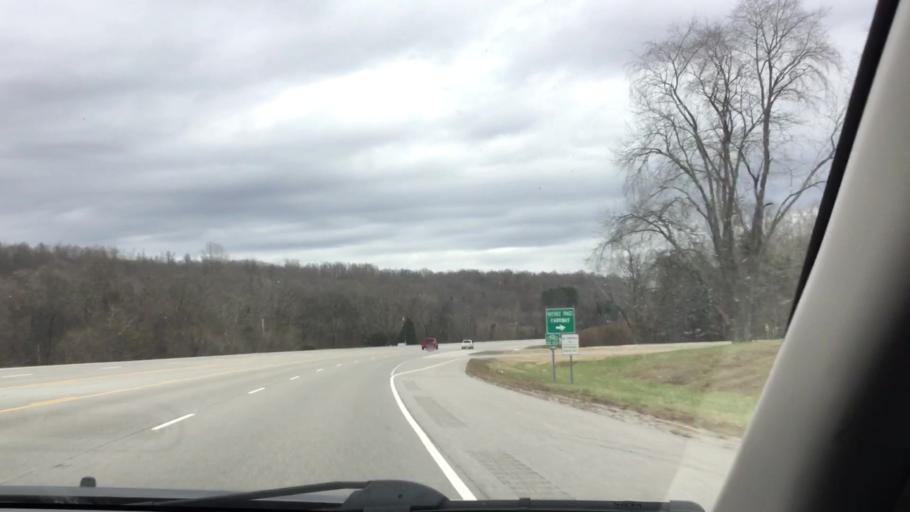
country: US
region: Tennessee
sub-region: Lewis County
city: Hohenwald
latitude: 35.5769
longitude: -87.4311
